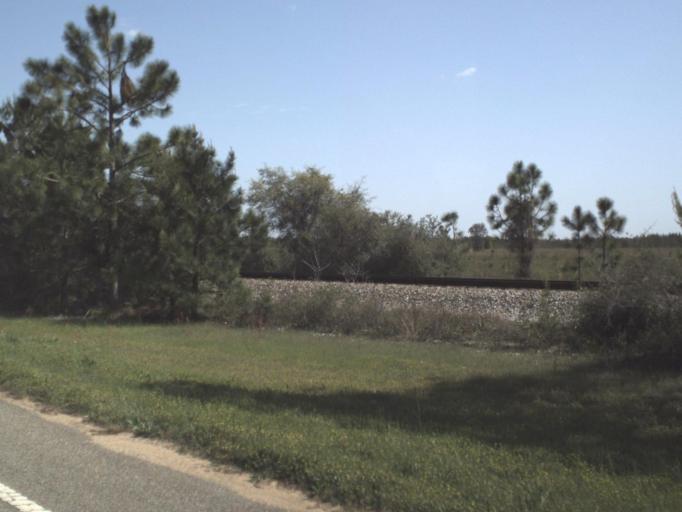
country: US
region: Florida
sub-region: Okaloosa County
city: Crestview
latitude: 30.7490
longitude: -86.4244
